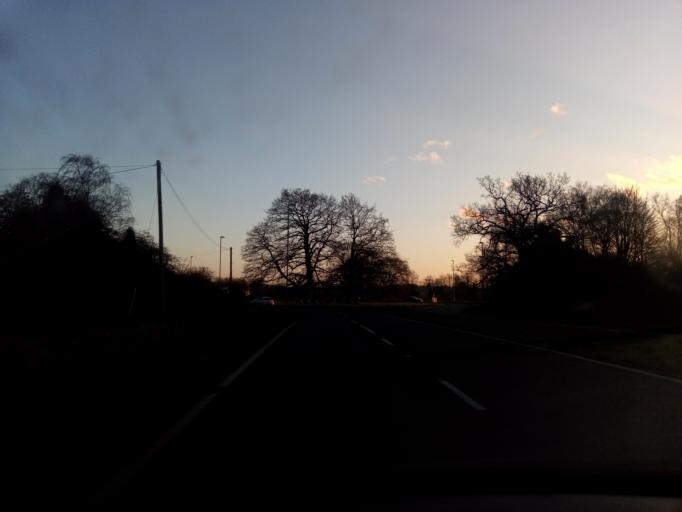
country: GB
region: England
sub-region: Nottinghamshire
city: Farnsfield
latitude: 53.0530
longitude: -1.0685
